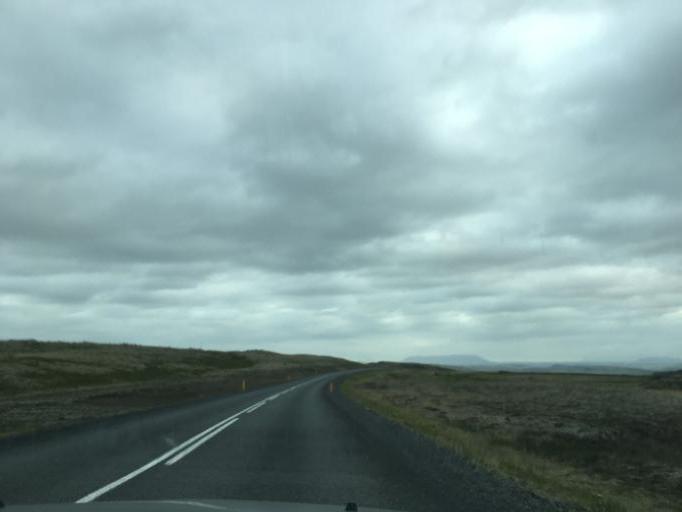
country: IS
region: South
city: Vestmannaeyjar
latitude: 64.2444
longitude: -20.2139
